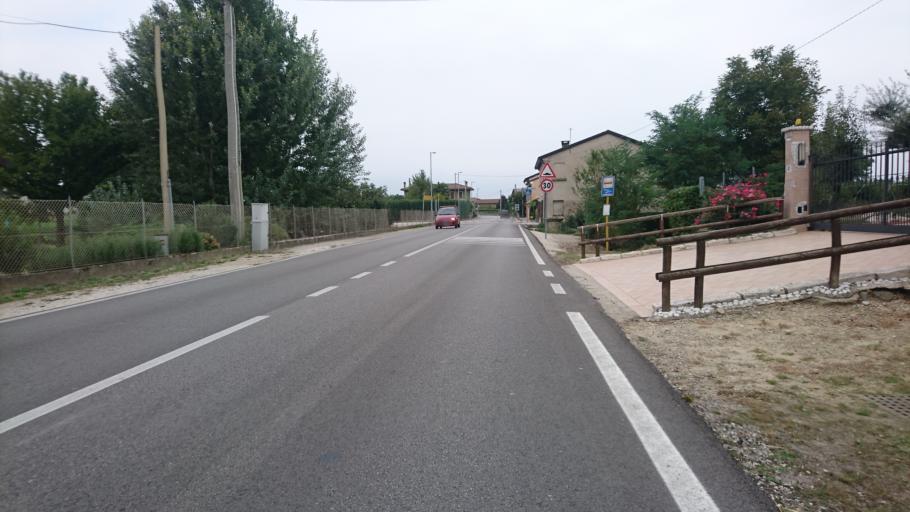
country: IT
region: Veneto
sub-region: Provincia di Padova
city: Curtarolo
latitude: 45.5328
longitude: 11.8398
